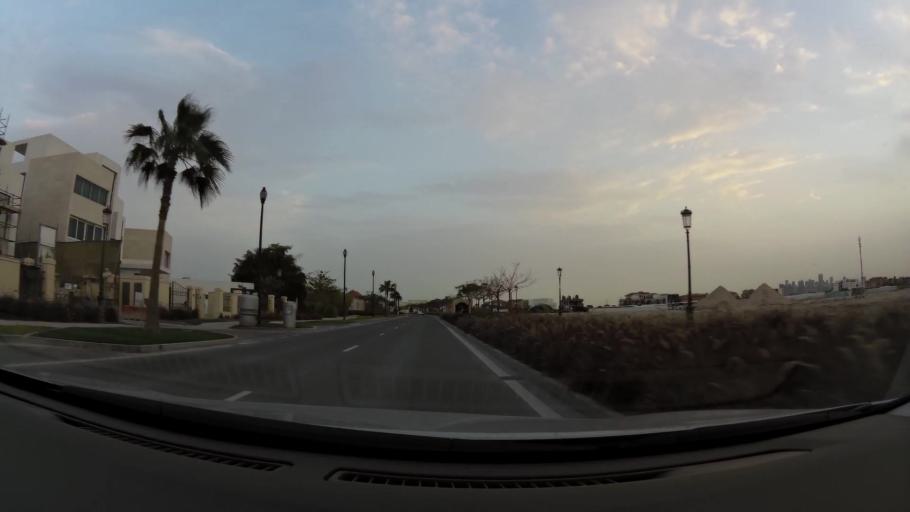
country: QA
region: Baladiyat ad Dawhah
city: Doha
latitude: 25.3653
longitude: 51.5641
